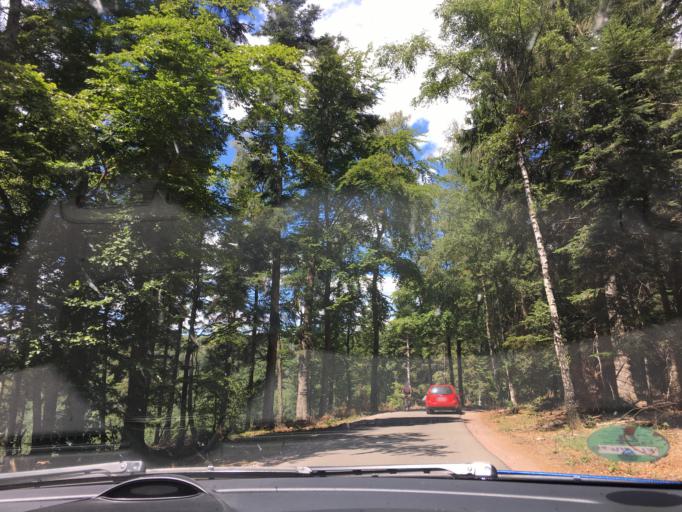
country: DE
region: Rheinland-Pfalz
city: Hauenstein
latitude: 49.2428
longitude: 7.8282
